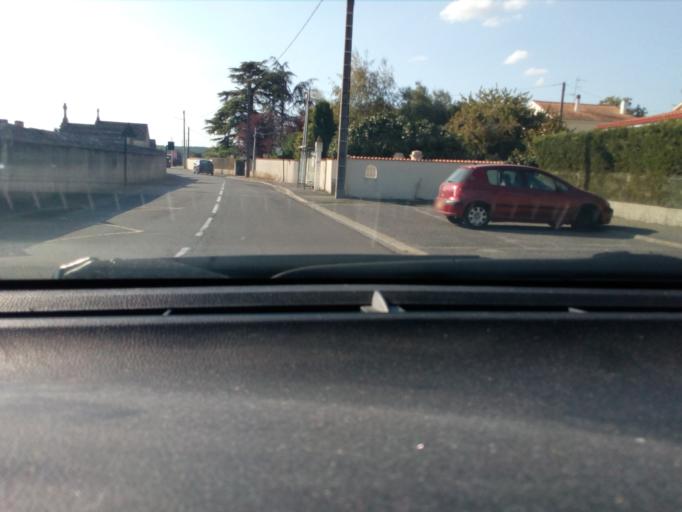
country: FR
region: Poitou-Charentes
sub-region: Departement de la Charente
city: Angouleme
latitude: 45.6647
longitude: 0.1407
